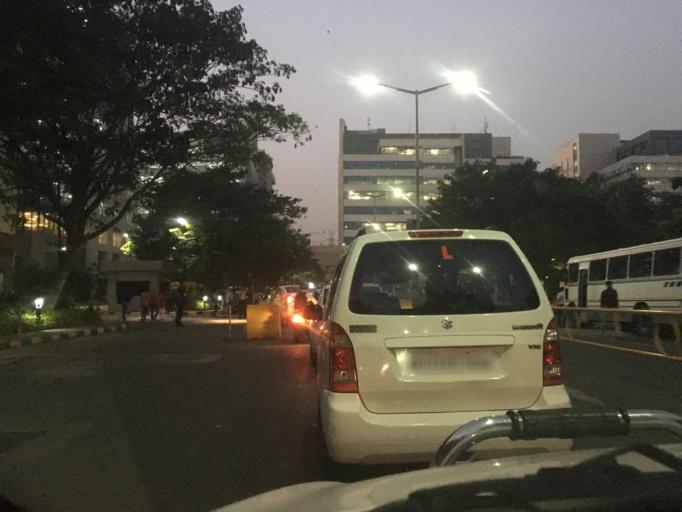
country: IN
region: Maharashtra
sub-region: Thane
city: Airoli
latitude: 19.1615
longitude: 73.0019
